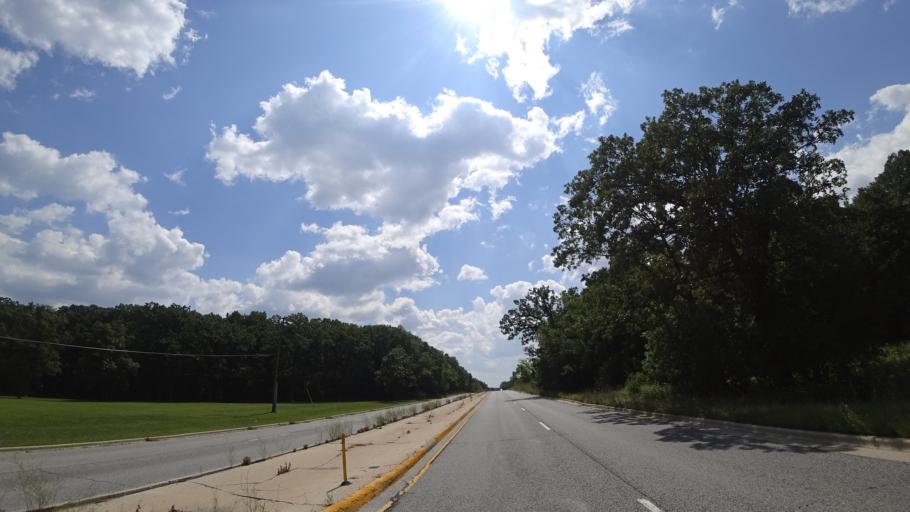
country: US
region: Illinois
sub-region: Cook County
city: Palos Heights
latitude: 41.6398
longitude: -87.7956
